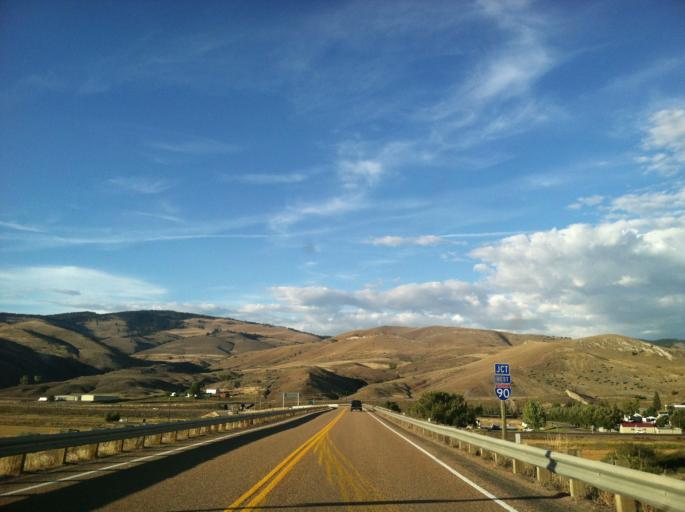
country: US
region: Montana
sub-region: Granite County
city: Philipsburg
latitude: 46.6673
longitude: -113.1546
